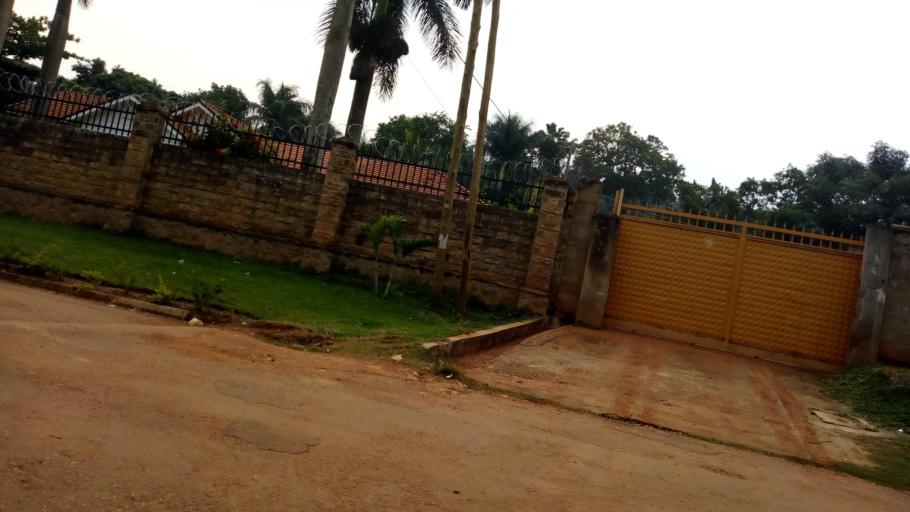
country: UG
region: Central Region
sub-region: Wakiso District
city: Kireka
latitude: 0.3213
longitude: 32.6291
